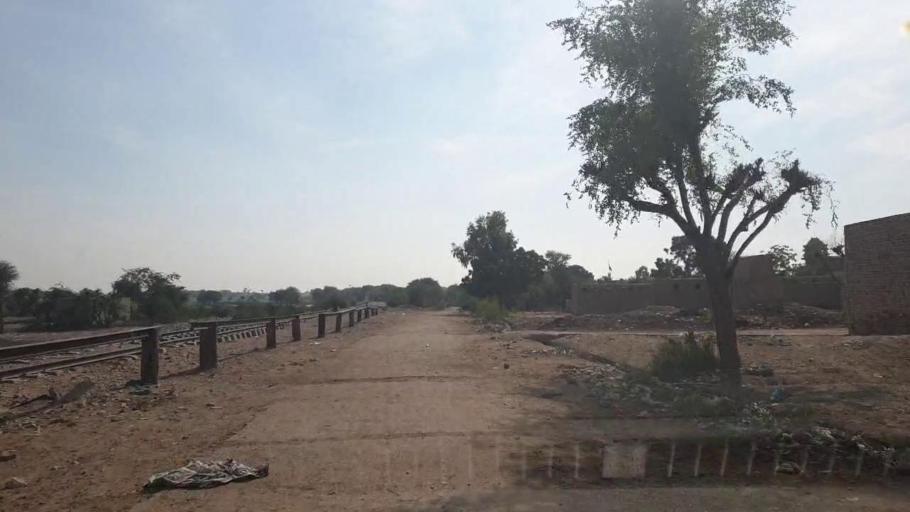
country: PK
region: Sindh
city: Hala
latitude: 25.7437
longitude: 68.2946
